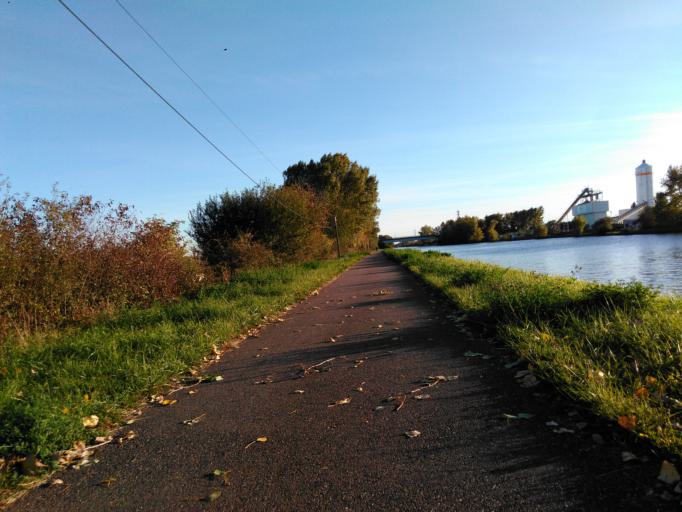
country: FR
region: Lorraine
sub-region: Departement de la Moselle
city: Talange
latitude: 49.2226
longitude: 6.1831
